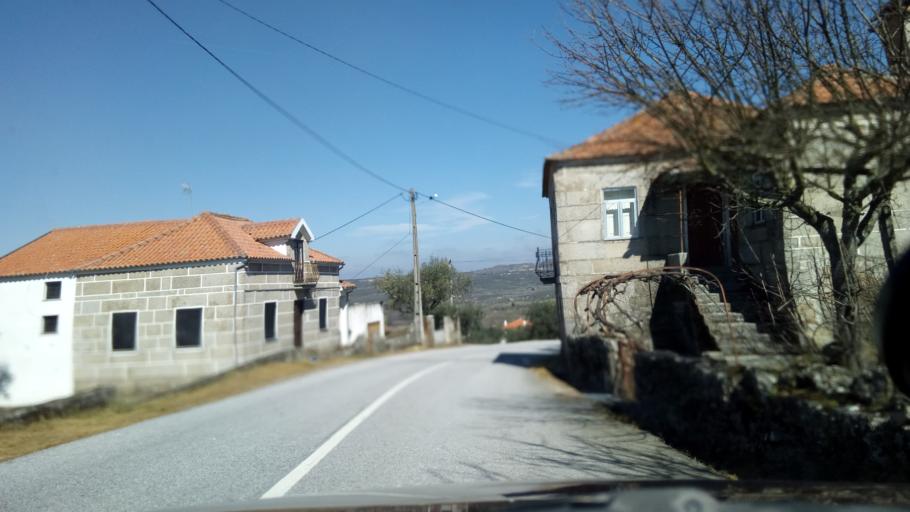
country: PT
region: Guarda
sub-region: Fornos de Algodres
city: Fornos de Algodres
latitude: 40.6545
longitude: -7.5338
